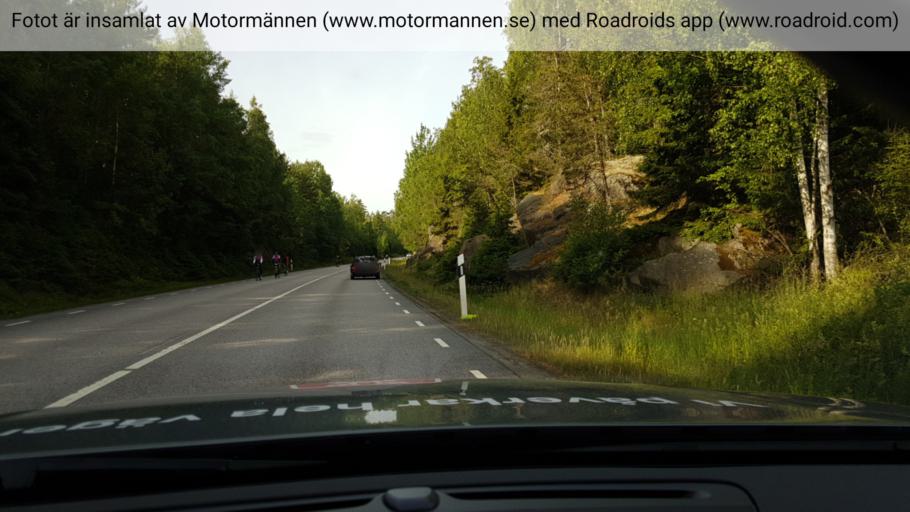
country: SE
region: Vaestra Goetaland
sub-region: Karlsborgs Kommun
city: Karlsborg
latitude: 58.6887
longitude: 14.6743
